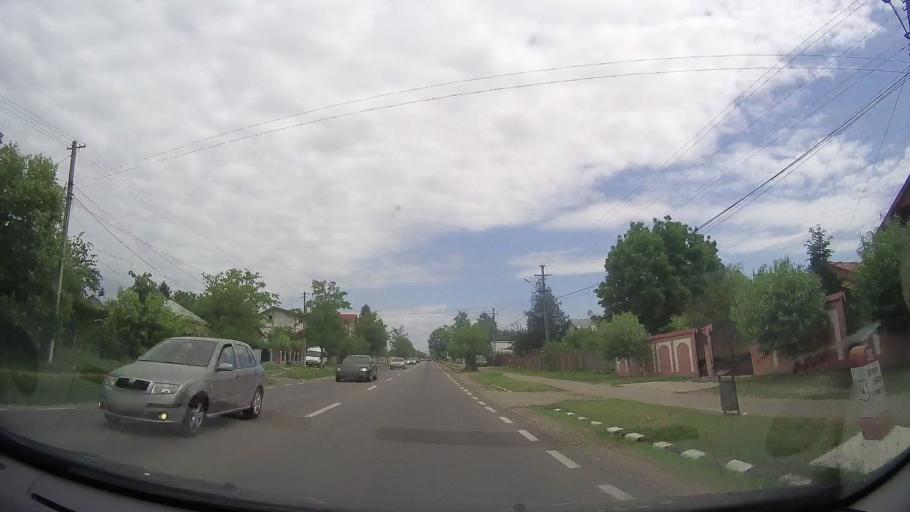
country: RO
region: Prahova
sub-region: Comuna Lipanesti
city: Sipotu
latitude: 45.0451
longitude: 26.0188
